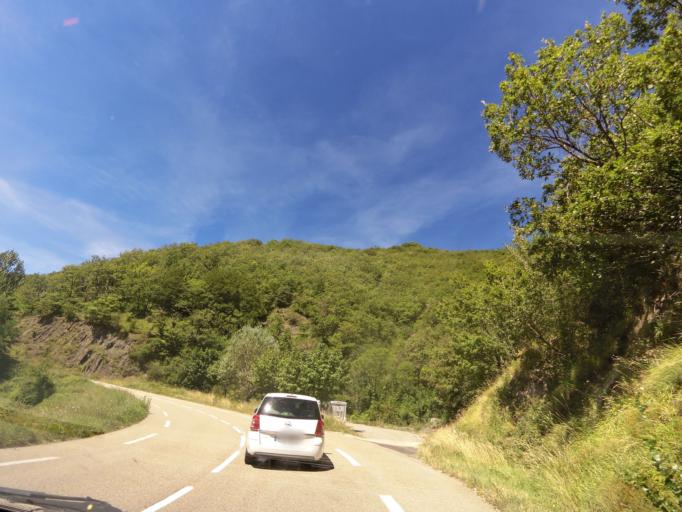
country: FR
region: Languedoc-Roussillon
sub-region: Departement du Gard
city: Le Vigan
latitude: 43.9739
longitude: 3.4557
